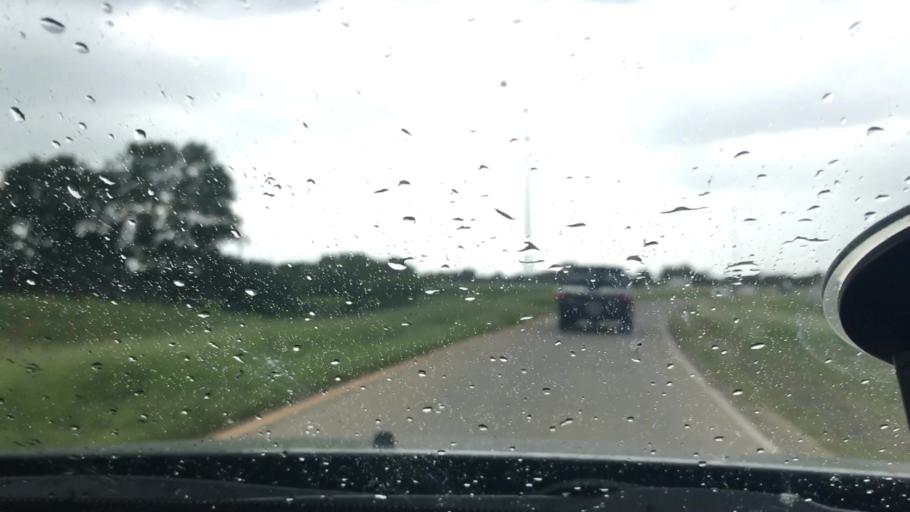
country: US
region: Oklahoma
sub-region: Okmulgee County
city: Henryetta
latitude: 35.4348
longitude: -95.9717
